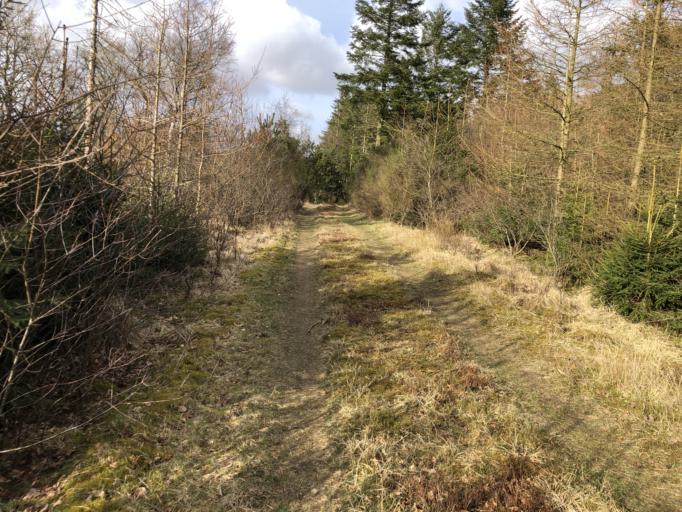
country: DK
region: Central Jutland
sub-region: Holstebro Kommune
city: Ulfborg
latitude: 56.2715
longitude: 8.4386
